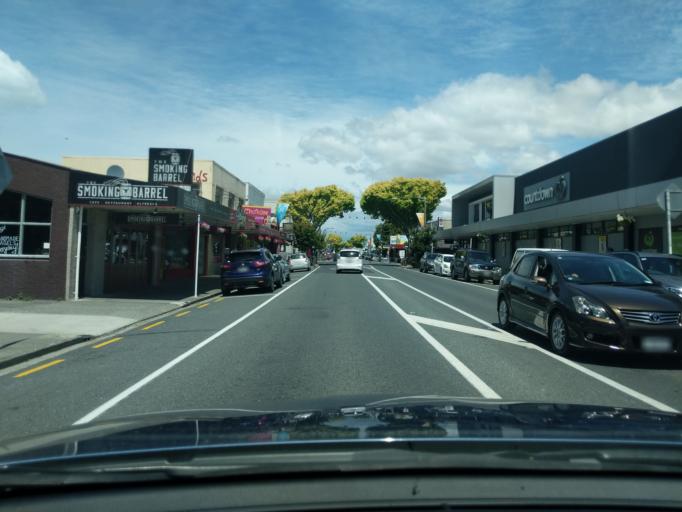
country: NZ
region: Tasman
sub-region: Tasman District
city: Motueka
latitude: -41.1093
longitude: 173.0112
